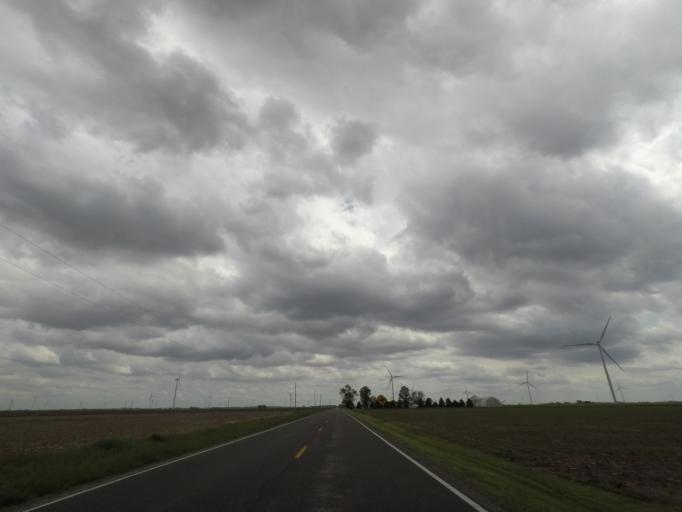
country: US
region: Illinois
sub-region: Macon County
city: Warrensburg
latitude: 40.0225
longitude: -89.0855
